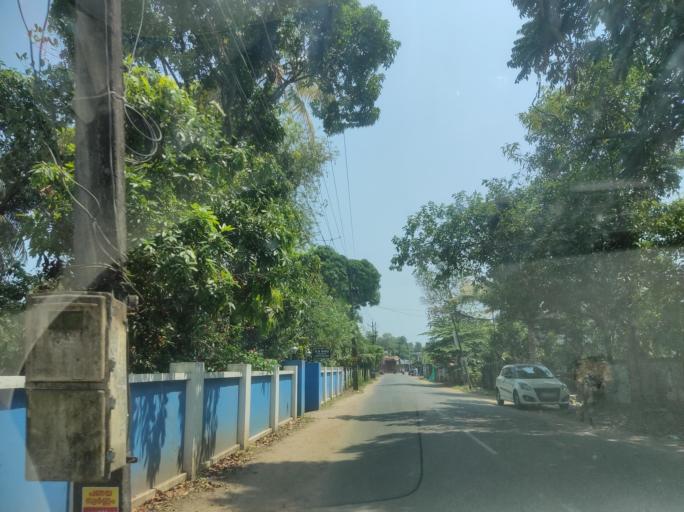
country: IN
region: Kerala
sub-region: Alappuzha
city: Kutiatodu
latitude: 9.7756
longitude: 76.3055
